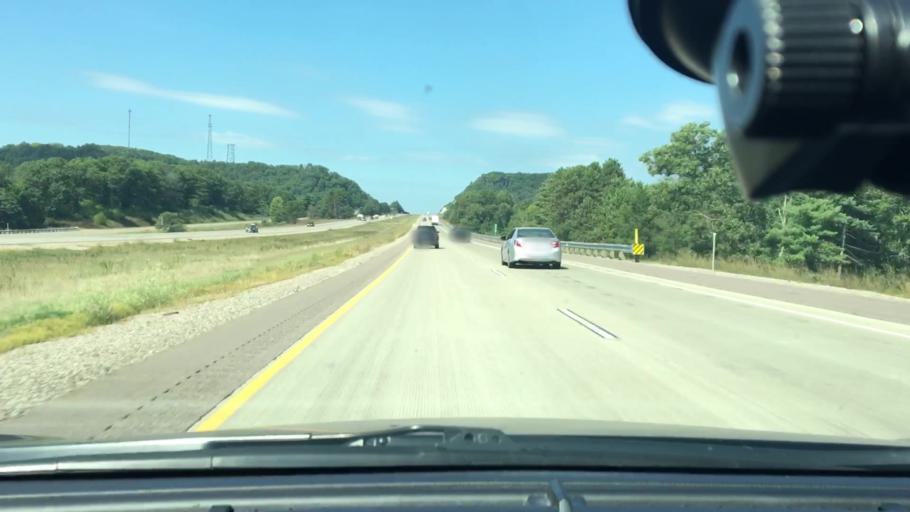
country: US
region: Wisconsin
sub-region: Jackson County
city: Black River Falls
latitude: 44.3332
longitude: -90.8968
